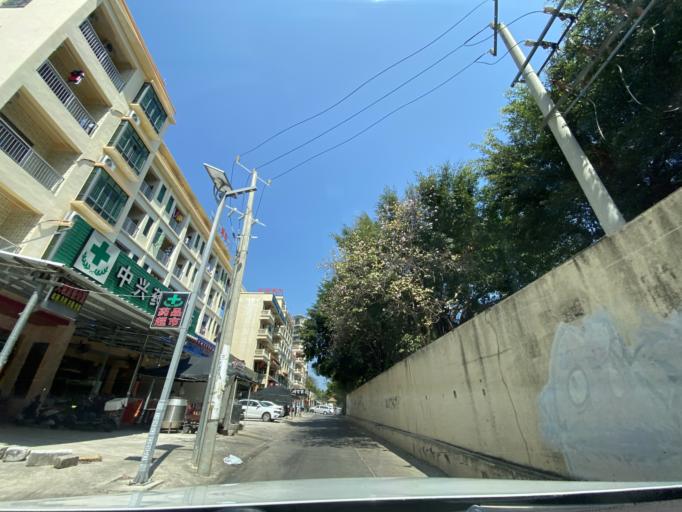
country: CN
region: Hainan
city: Yingzhou
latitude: 18.4040
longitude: 109.8453
